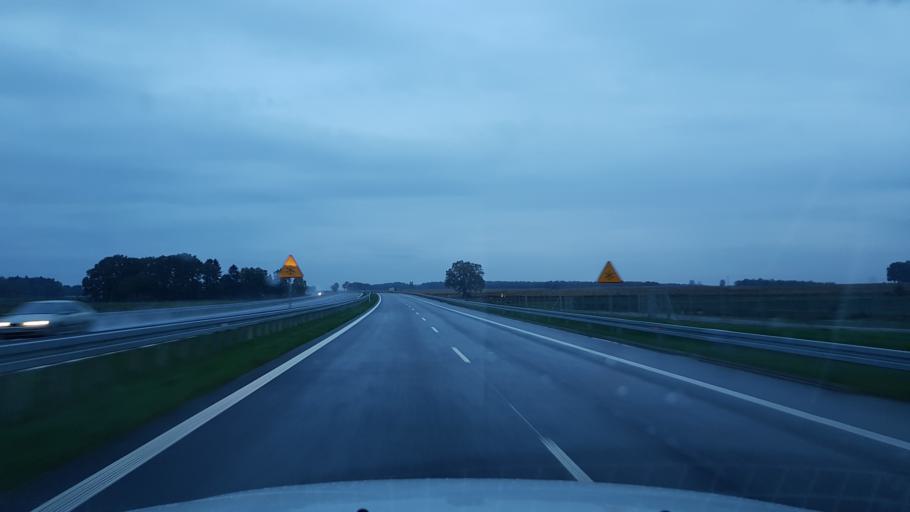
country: PL
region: West Pomeranian Voivodeship
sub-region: Powiat gryficki
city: Brojce
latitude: 53.8939
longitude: 15.3827
